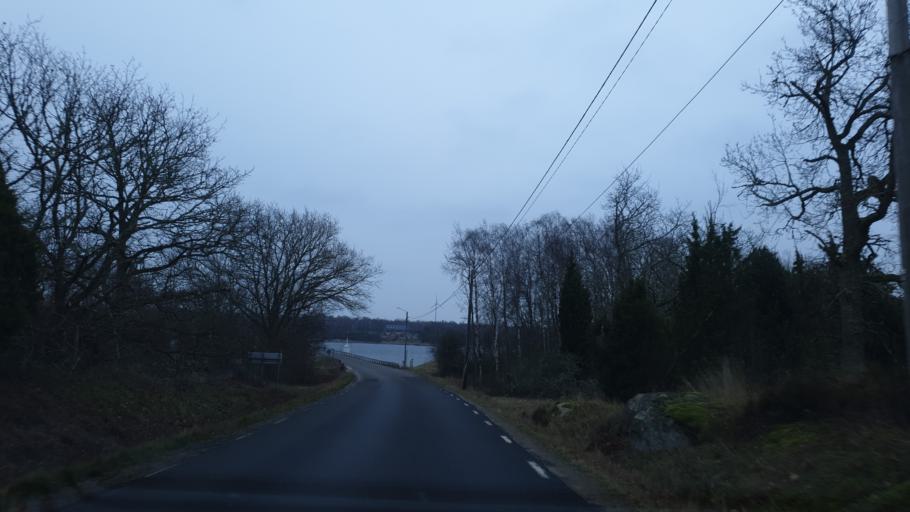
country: SE
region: Blekinge
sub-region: Karlskrona Kommun
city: Karlskrona
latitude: 56.1071
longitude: 15.6316
